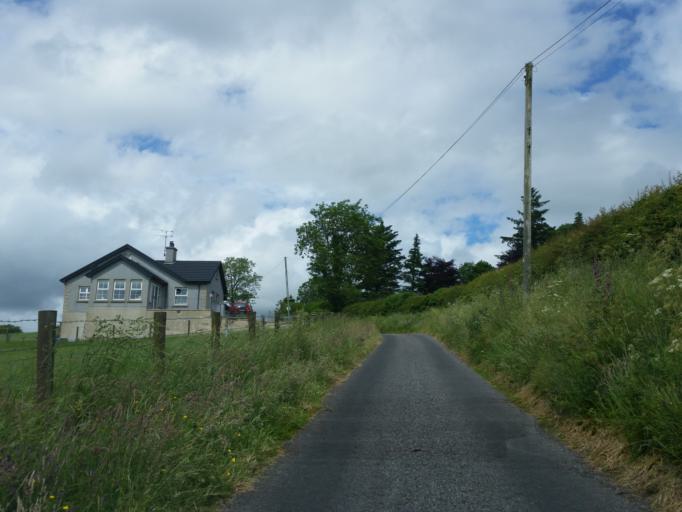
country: GB
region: Northern Ireland
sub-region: Omagh District
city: Omagh
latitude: 54.5479
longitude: -7.0841
